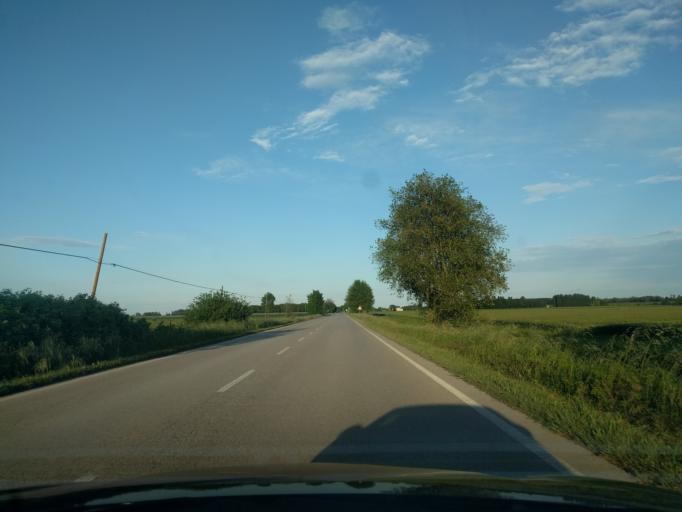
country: IT
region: Veneto
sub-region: Provincia di Rovigo
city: Guarda Veneta
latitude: 44.9833
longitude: 11.8240
